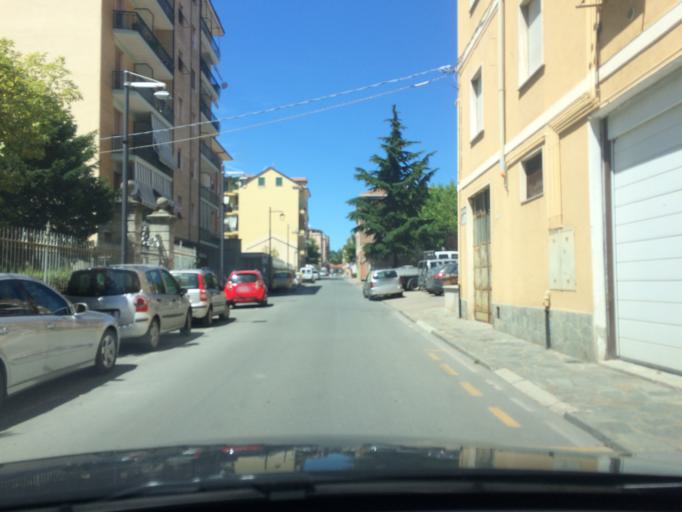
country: IT
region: Piedmont
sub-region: Provincia di Alessandria
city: Acqui Terme
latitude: 44.6753
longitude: 8.4645
